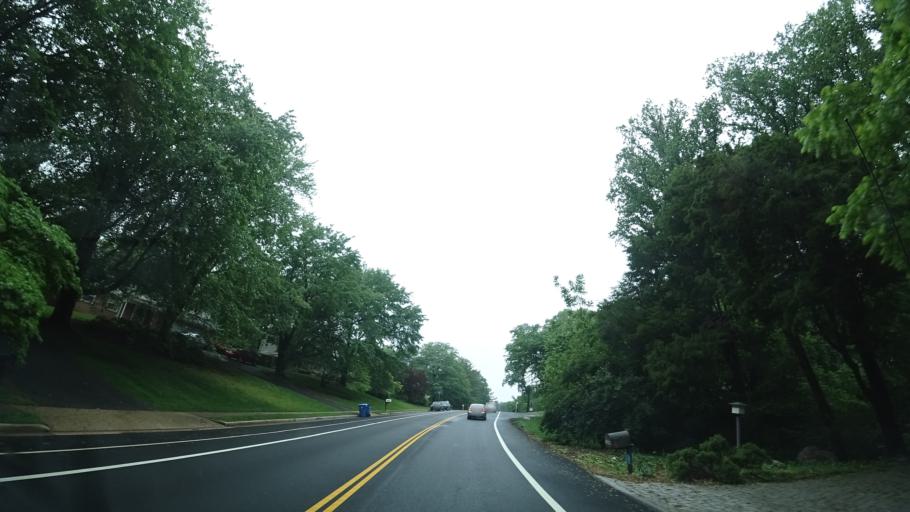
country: US
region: Virginia
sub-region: Fairfax County
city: Tysons Corner
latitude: 38.9408
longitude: -77.2174
